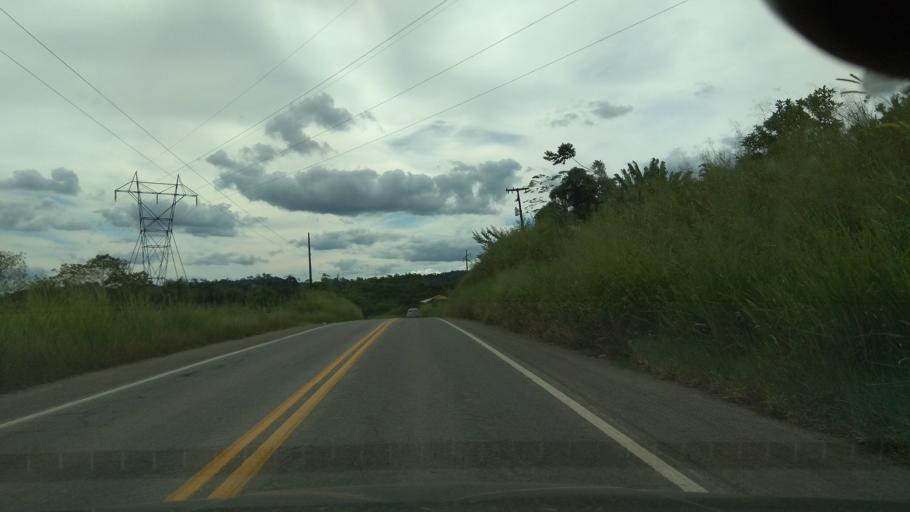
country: BR
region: Bahia
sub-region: Ipiau
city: Ipiau
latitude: -14.1513
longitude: -39.6993
